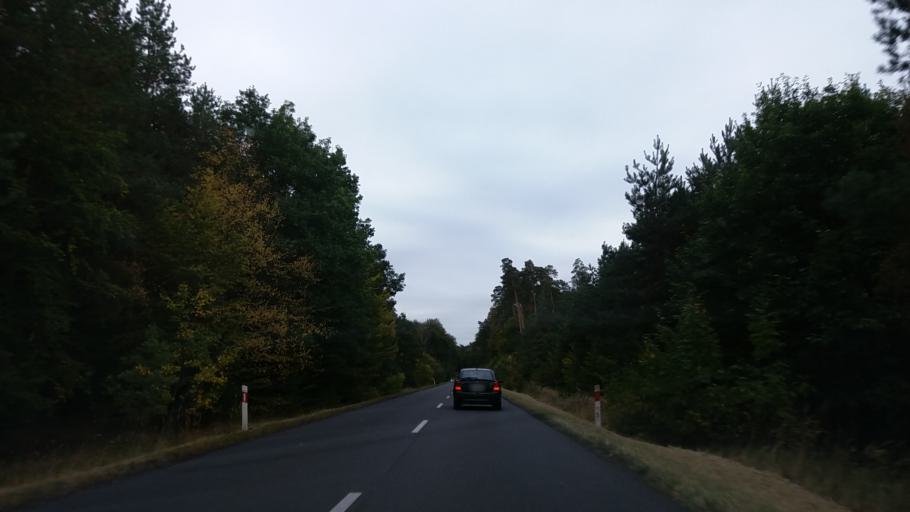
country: PL
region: Lubusz
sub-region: Powiat gorzowski
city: Klodawa
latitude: 52.8478
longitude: 15.1999
